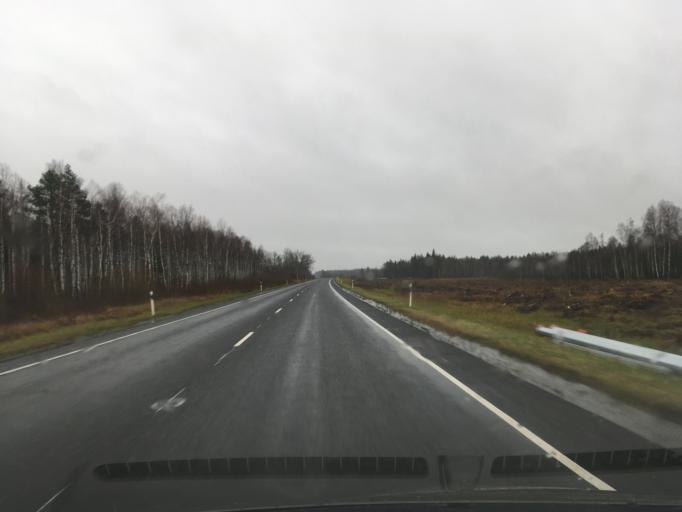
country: EE
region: Harju
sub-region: Nissi vald
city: Turba
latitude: 58.9491
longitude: 24.0833
